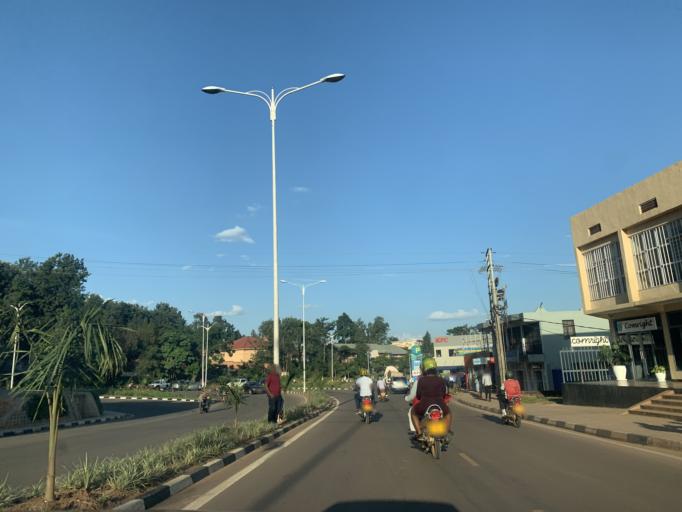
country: RW
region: Kigali
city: Kigali
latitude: -1.9600
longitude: 30.1163
